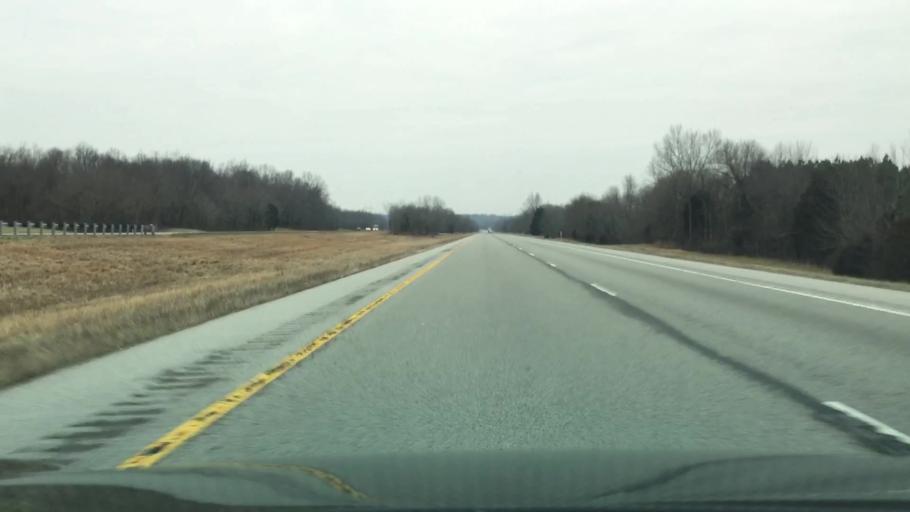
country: US
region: Illinois
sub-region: Johnson County
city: Vienna
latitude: 37.3555
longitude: -88.7903
